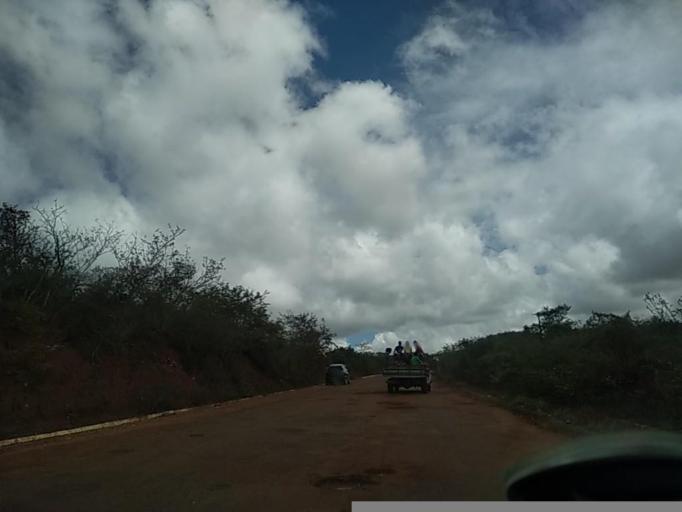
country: BR
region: Bahia
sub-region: Caetite
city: Caetite
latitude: -14.0286
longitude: -42.4880
